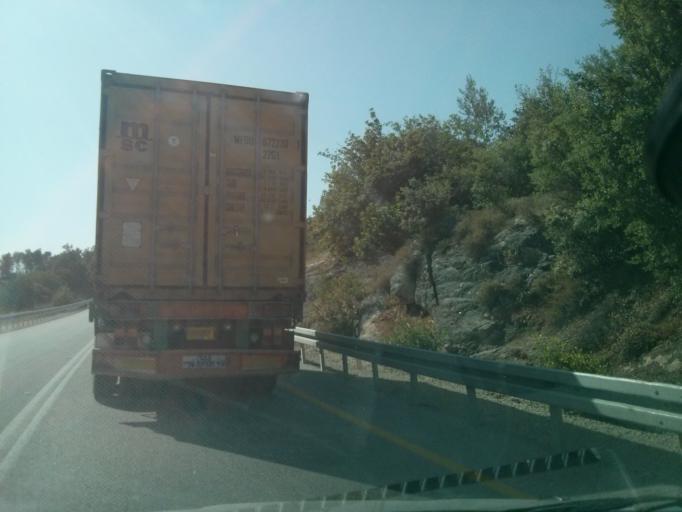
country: IL
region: Jerusalem
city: Bet Shemesh
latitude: 31.6755
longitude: 35.0088
